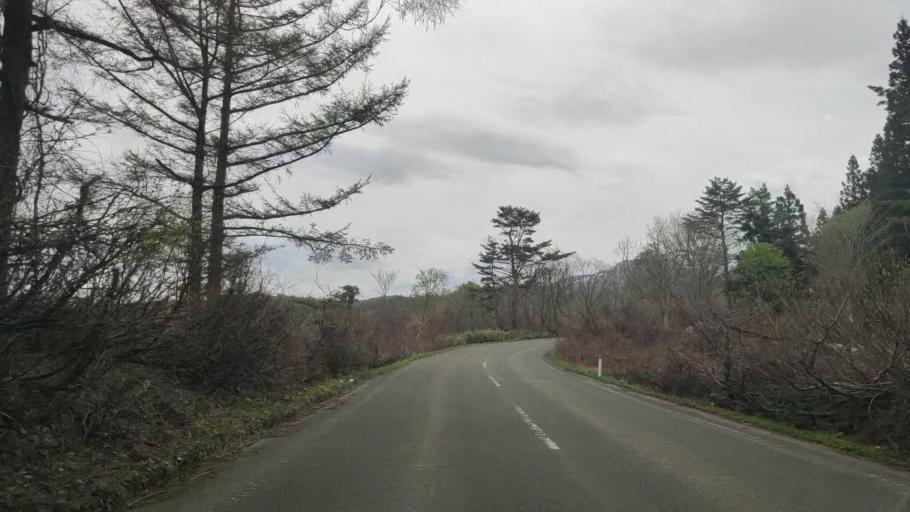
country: JP
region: Aomori
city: Aomori Shi
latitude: 40.7274
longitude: 140.8483
